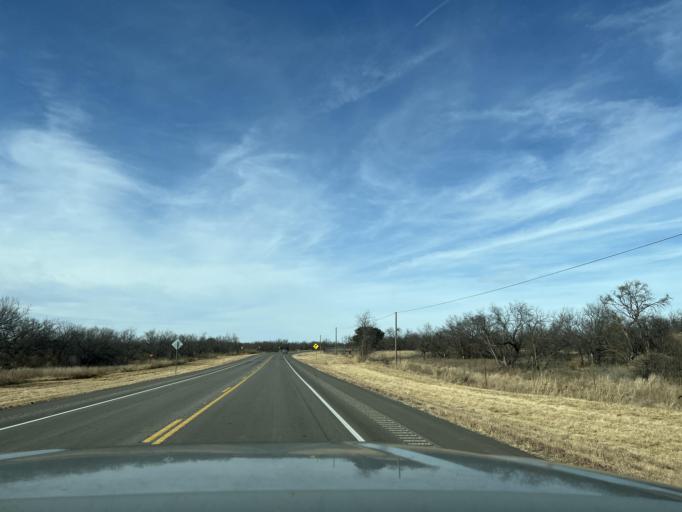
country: US
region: Texas
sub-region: Shackelford County
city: Albany
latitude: 32.6271
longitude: -99.2233
